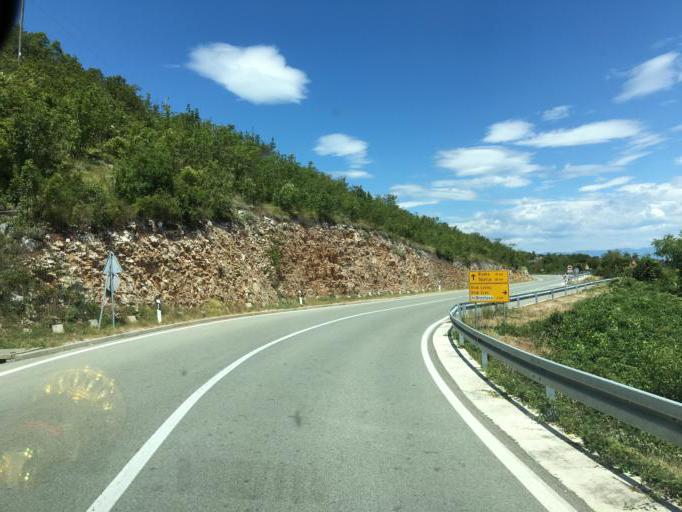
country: HR
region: Istarska
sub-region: Grad Labin
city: Rabac
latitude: 45.1538
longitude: 14.2129
